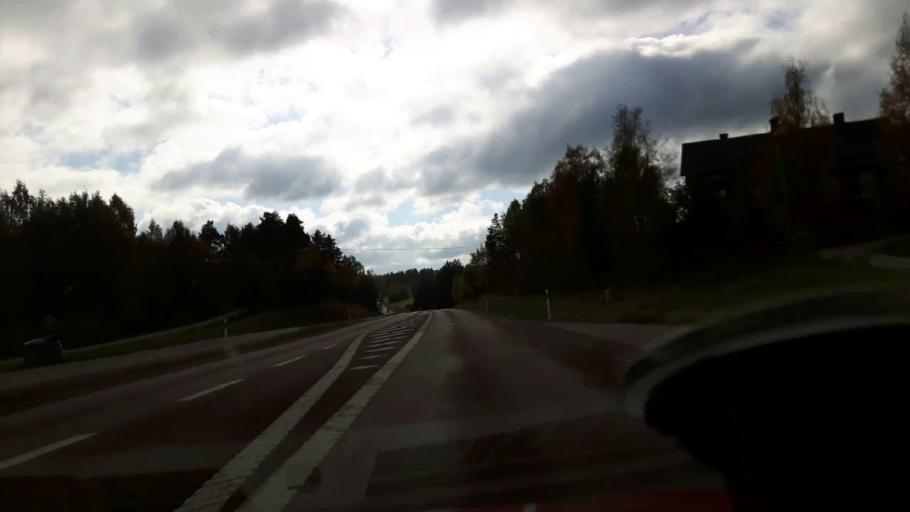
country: SE
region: Gaevleborg
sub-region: Ljusdals Kommun
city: Jaervsoe
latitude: 61.6716
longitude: 16.1457
